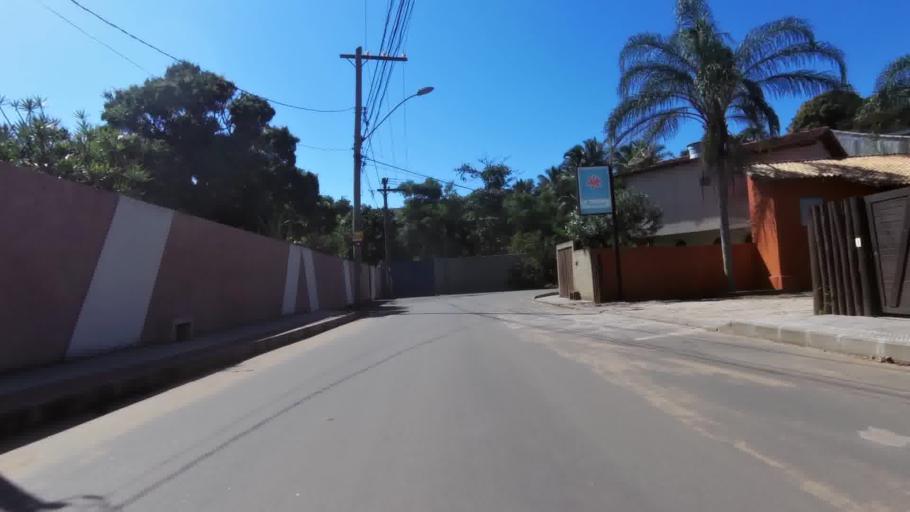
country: BR
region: Espirito Santo
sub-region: Guarapari
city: Guarapari
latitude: -20.7381
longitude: -40.5372
